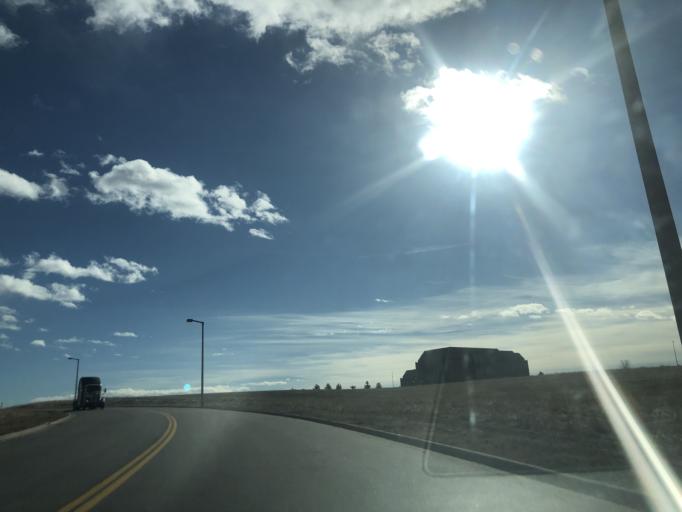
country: US
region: Colorado
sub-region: Douglas County
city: Meridian
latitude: 39.5542
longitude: -104.8567
